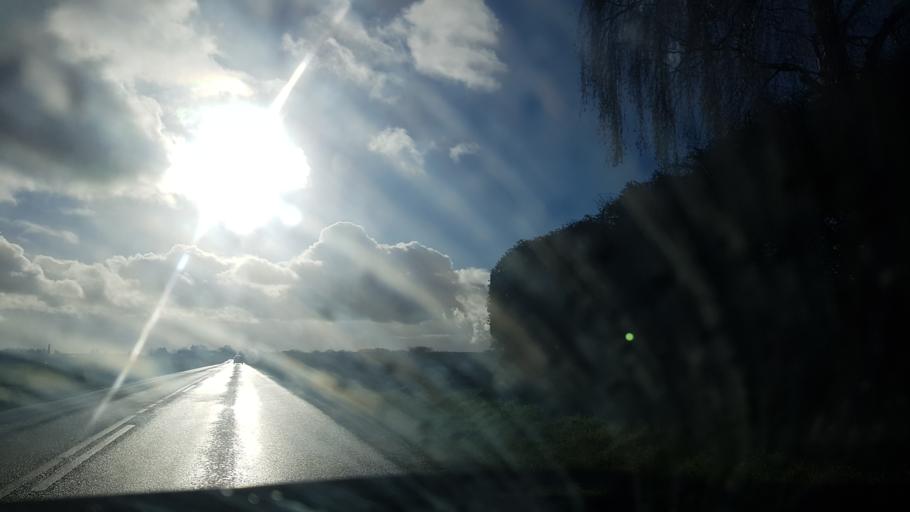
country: DK
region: South Denmark
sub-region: Fredericia Kommune
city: Taulov
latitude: 55.5267
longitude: 9.6394
